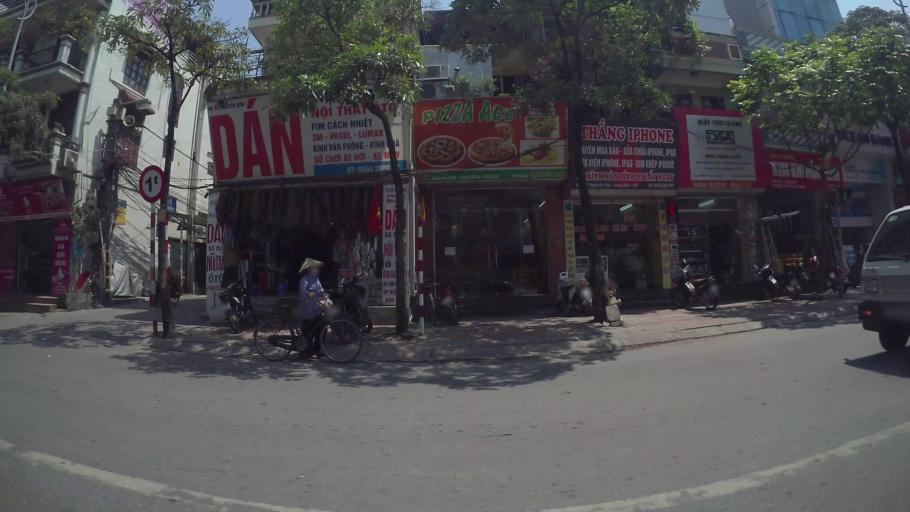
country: VN
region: Ha Noi
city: Hoan Kiem
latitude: 21.0471
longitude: 105.8778
